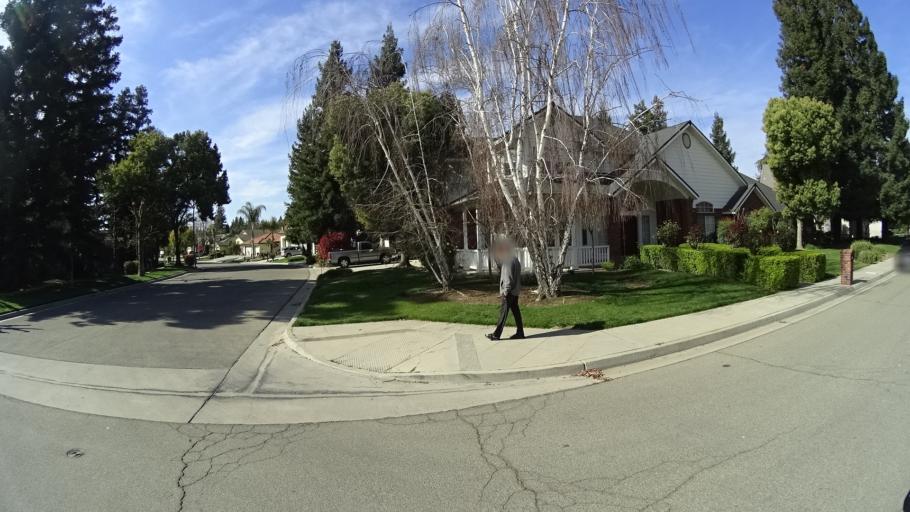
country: US
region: California
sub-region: Fresno County
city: West Park
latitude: 36.8443
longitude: -119.8783
